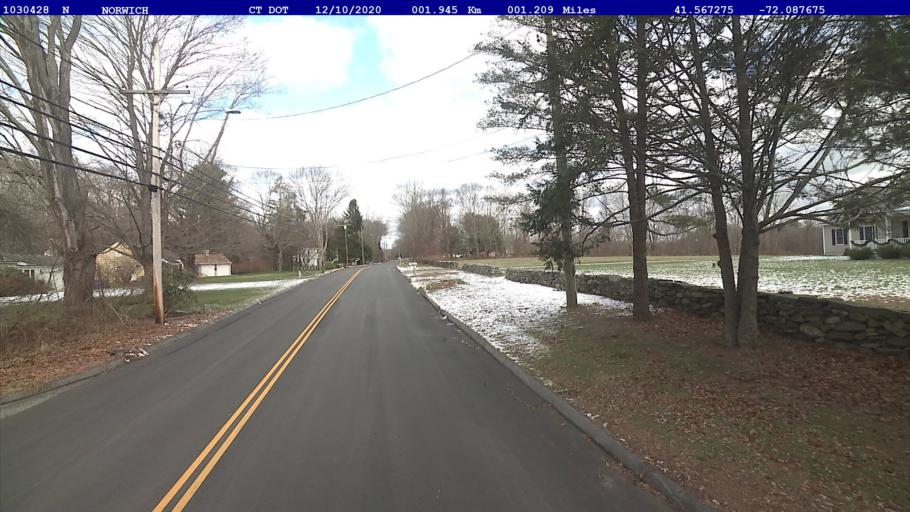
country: US
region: Connecticut
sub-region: New London County
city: Norwich
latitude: 41.5673
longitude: -72.0877
